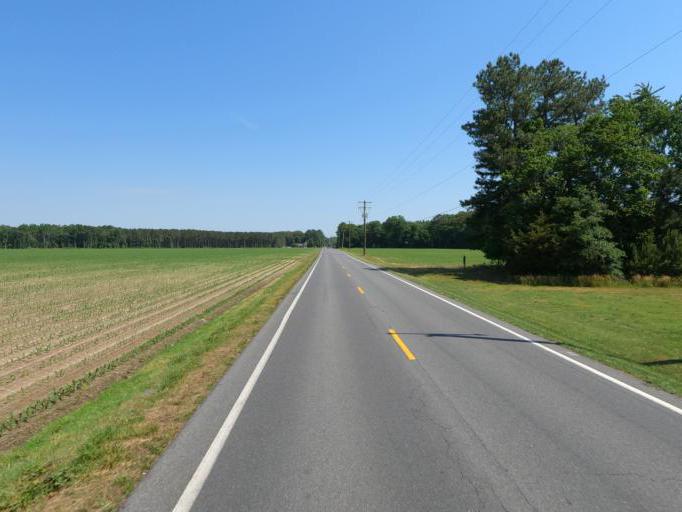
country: US
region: Delaware
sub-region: Sussex County
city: Georgetown
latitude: 38.6964
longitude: -75.3444
